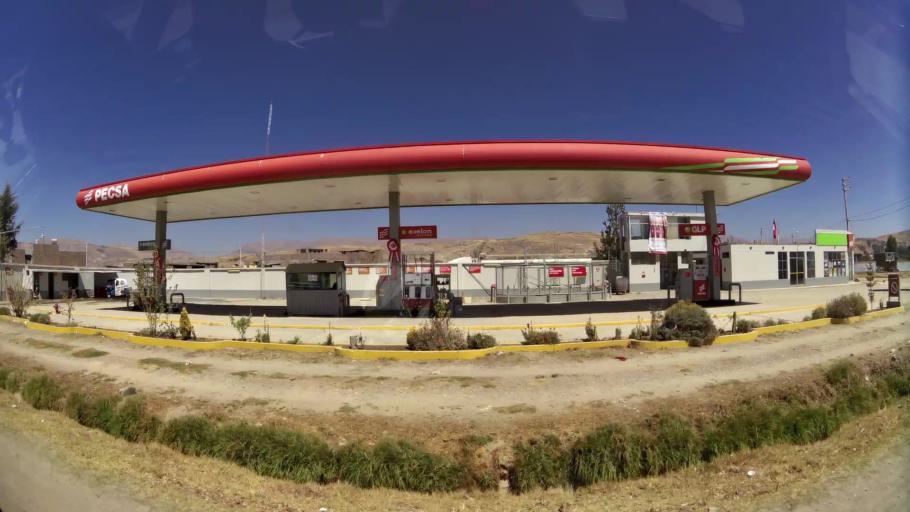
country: PE
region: Junin
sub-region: Provincia de Jauja
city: Jauja
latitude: -11.7735
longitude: -75.4893
